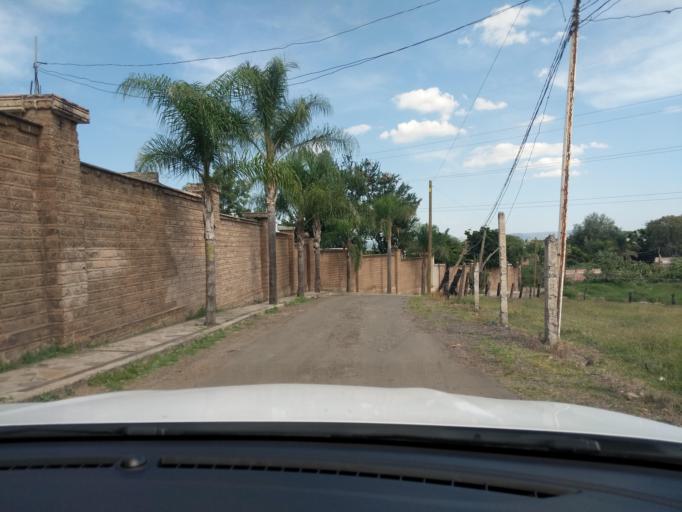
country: MX
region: Jalisco
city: Coyula
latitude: 20.6282
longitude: -103.2156
